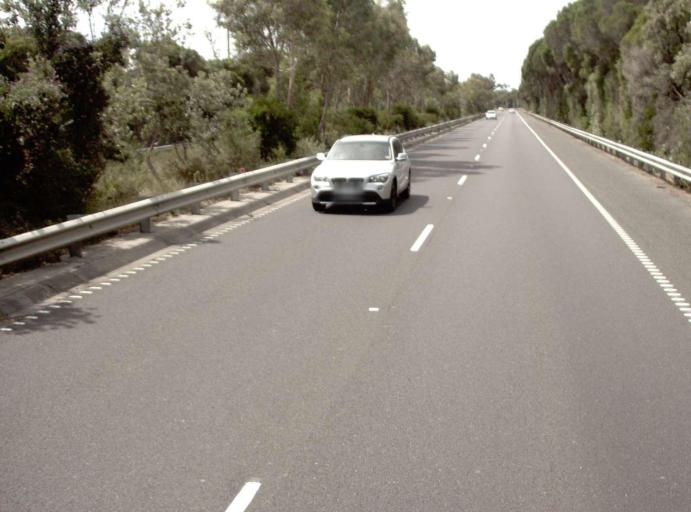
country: AU
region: Victoria
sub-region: Frankston
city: Frankston East
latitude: -38.1380
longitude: 145.1368
